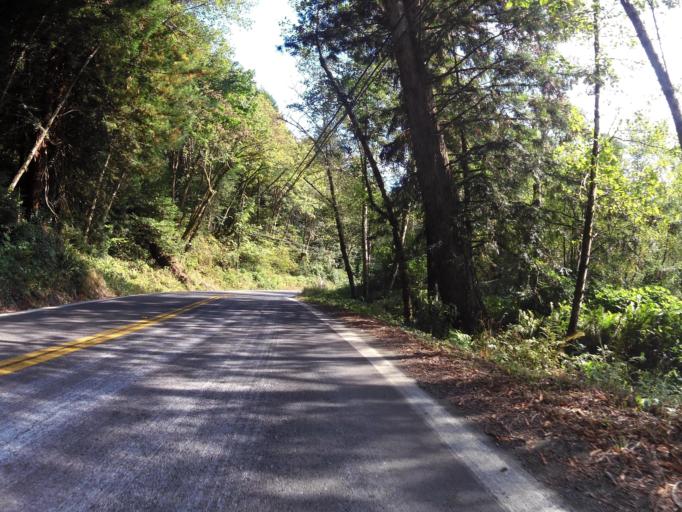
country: US
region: California
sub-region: Del Norte County
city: Bertsch-Oceanview
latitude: 41.8439
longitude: -124.1143
